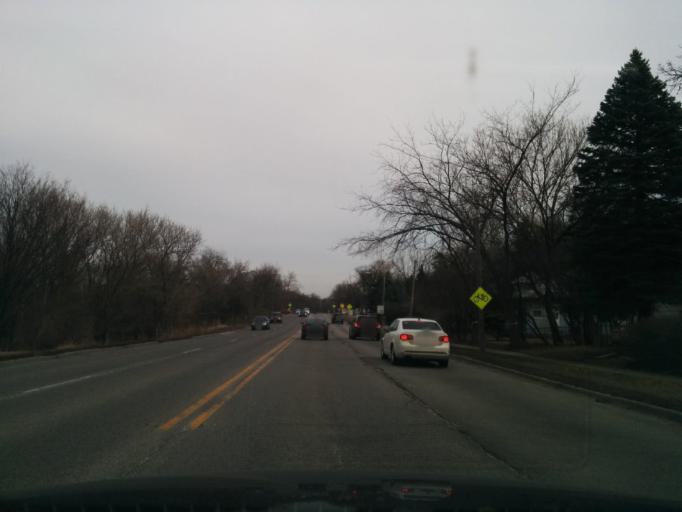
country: US
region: Illinois
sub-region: Cook County
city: Western Springs
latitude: 41.8199
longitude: -87.9059
